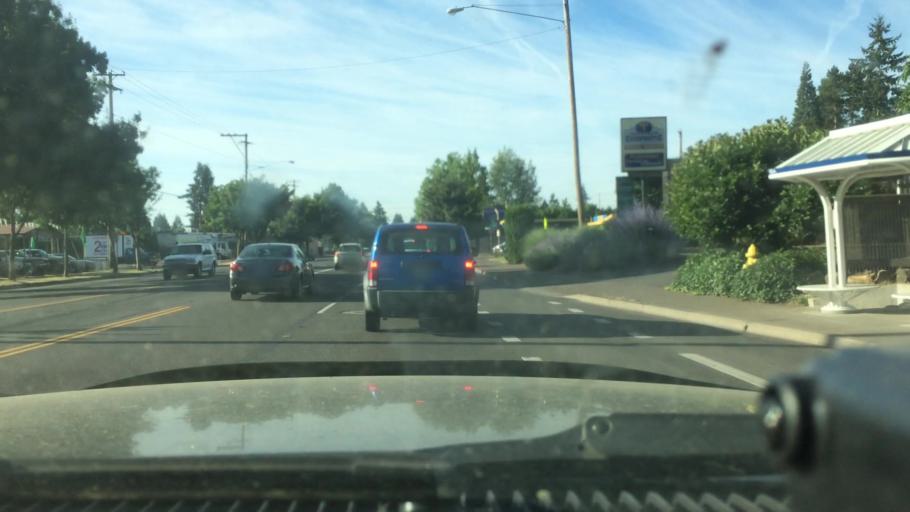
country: US
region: Oregon
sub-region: Lane County
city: Eugene
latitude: 44.0786
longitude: -123.1210
